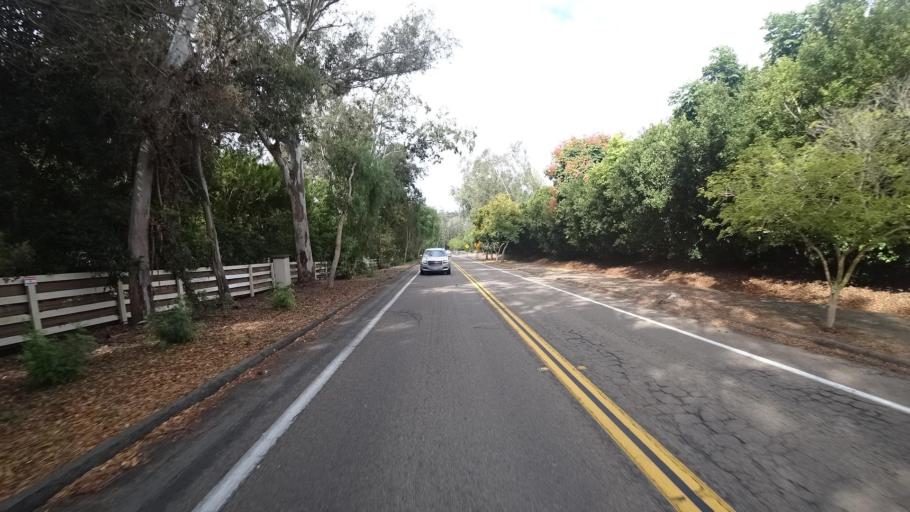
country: US
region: California
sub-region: San Diego County
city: Rancho Santa Fe
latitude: 33.0022
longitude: -117.2303
